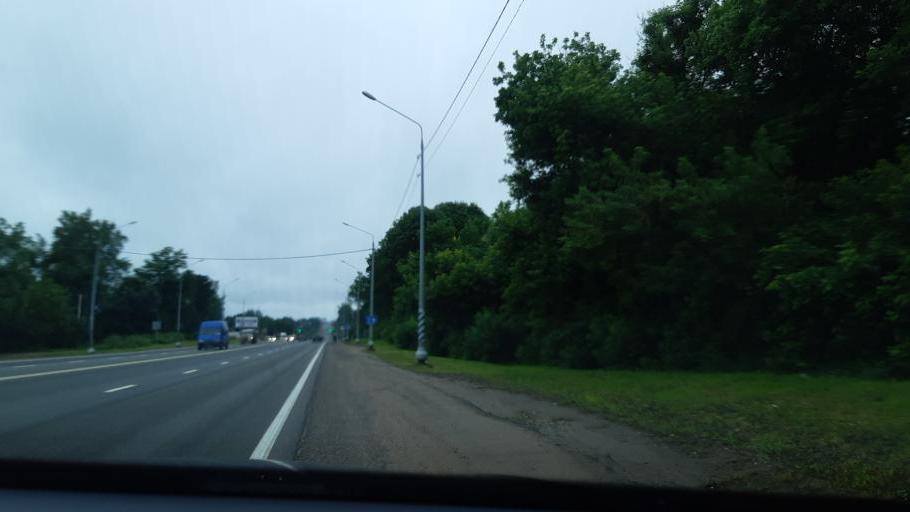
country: RU
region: Smolensk
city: Smolensk
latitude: 54.7171
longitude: 32.1073
